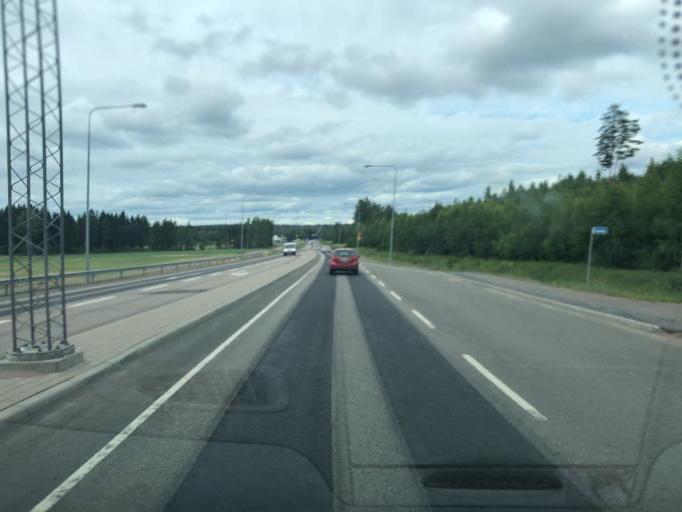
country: FI
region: Kymenlaakso
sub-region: Kouvola
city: Kouvola
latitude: 60.9220
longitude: 26.7900
